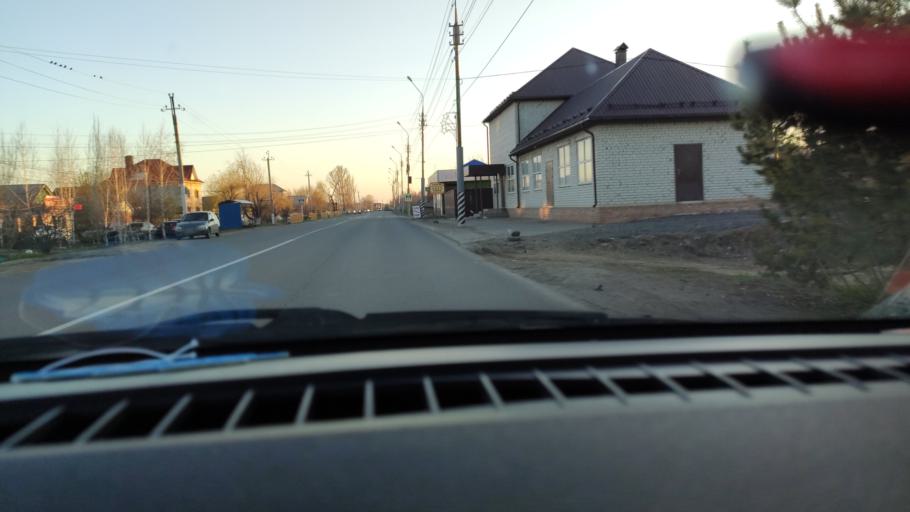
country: RU
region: Saratov
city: Privolzhskiy
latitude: 51.4297
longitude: 46.0534
